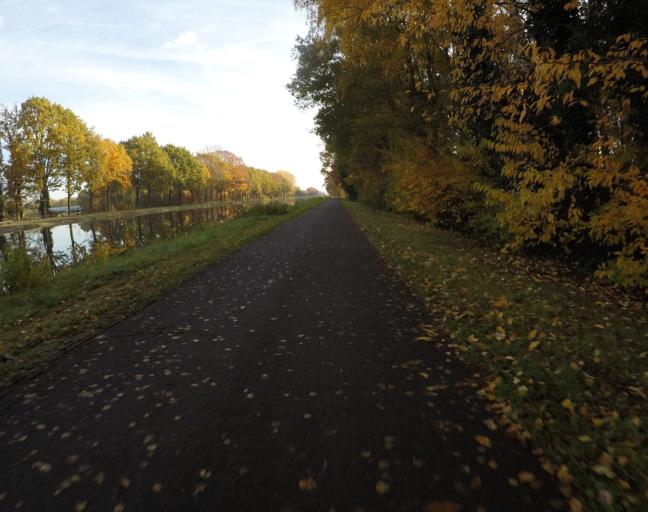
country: BE
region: Flanders
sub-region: Provincie Antwerpen
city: Geel
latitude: 51.2046
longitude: 5.0014
